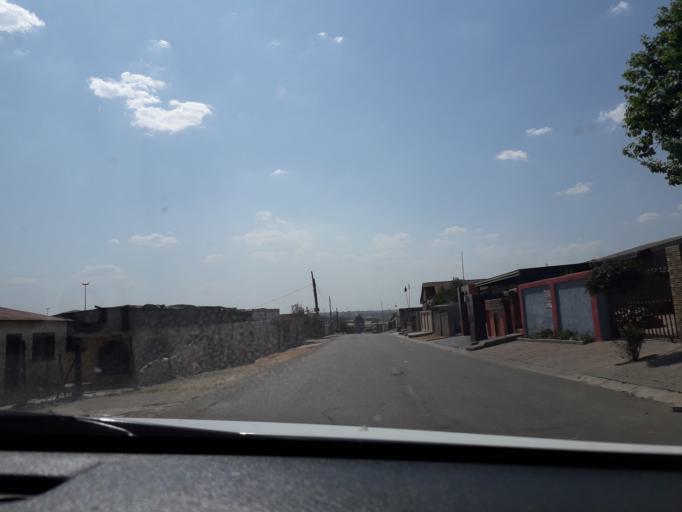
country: ZA
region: Gauteng
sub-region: Ekurhuleni Metropolitan Municipality
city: Tembisa
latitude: -26.0207
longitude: 28.2056
